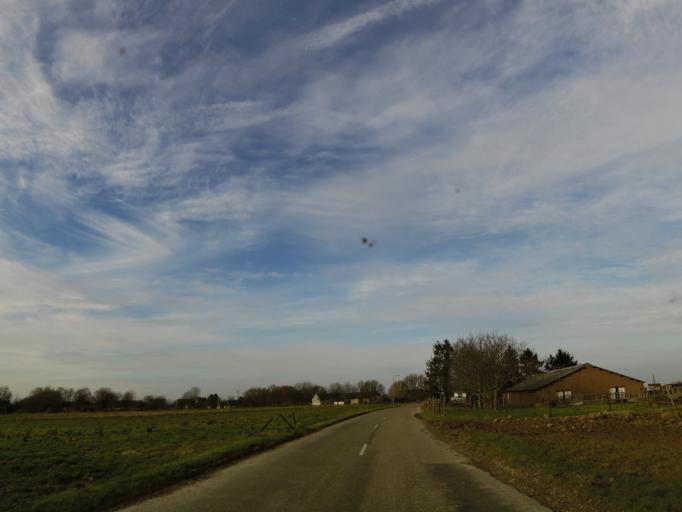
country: NL
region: Limburg
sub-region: Gemeente Voerendaal
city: Ubachsberg
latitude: 50.8412
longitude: 5.9249
